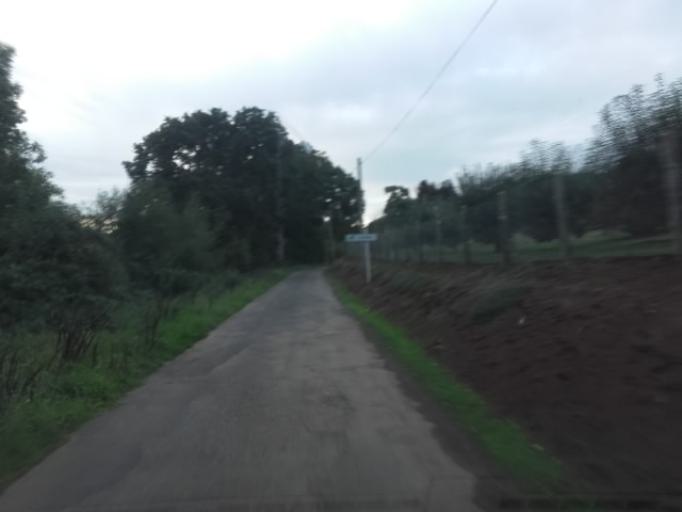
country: FR
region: Brittany
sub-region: Departement des Cotes-d'Armor
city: Pleguien
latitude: 48.6358
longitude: -2.9442
